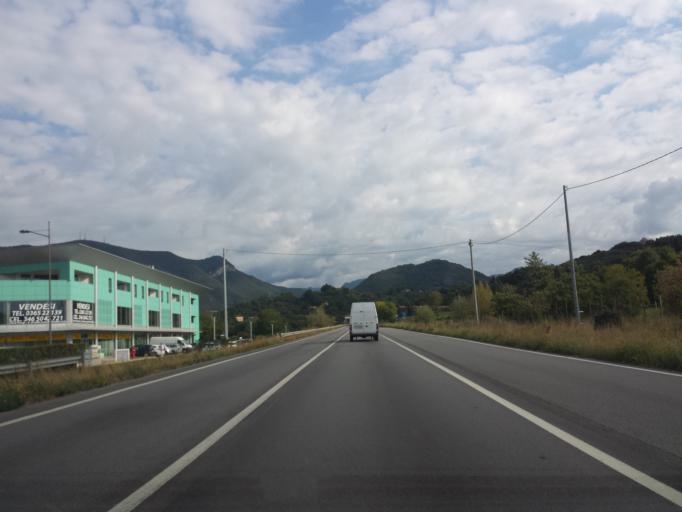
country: IT
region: Lombardy
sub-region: Provincia di Brescia
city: Gavardo-Sopraponte
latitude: 45.5774
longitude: 10.4453
